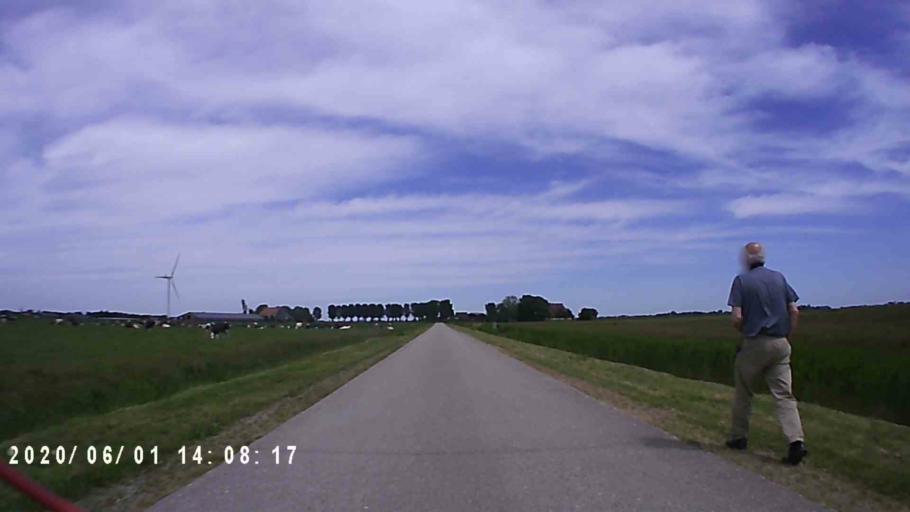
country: NL
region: Friesland
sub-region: Gemeente Littenseradiel
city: Winsum
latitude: 53.1199
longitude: 5.6416
